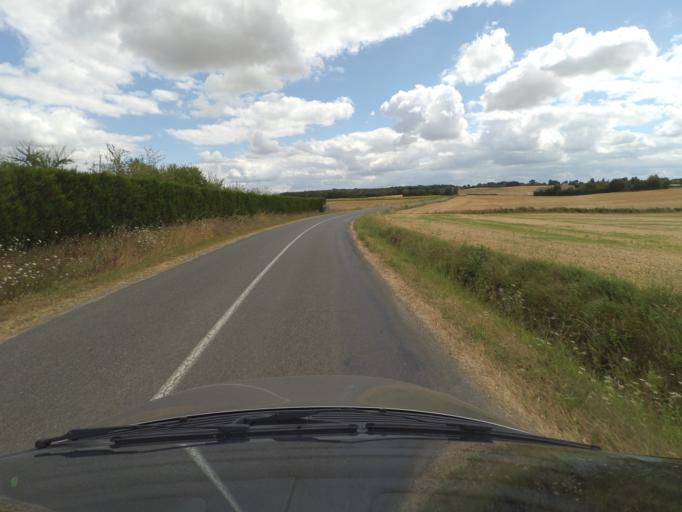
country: FR
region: Poitou-Charentes
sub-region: Departement de la Vienne
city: Saint-Savin
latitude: 46.5447
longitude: 0.9820
